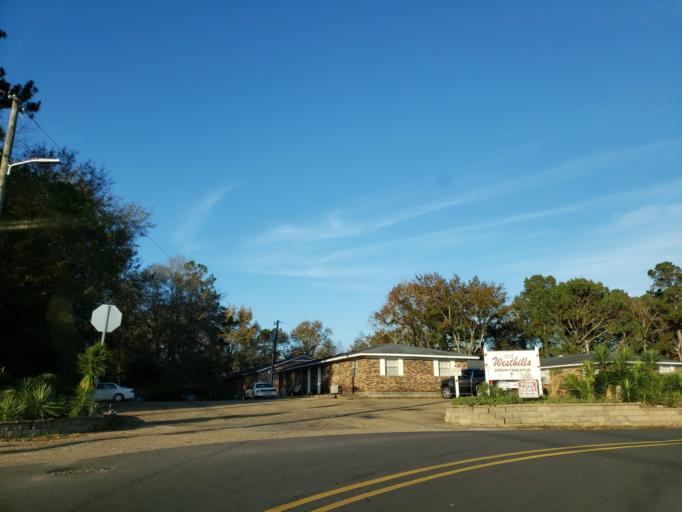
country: US
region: Mississippi
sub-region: Lamar County
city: Arnold Line
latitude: 31.3480
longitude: -89.3607
